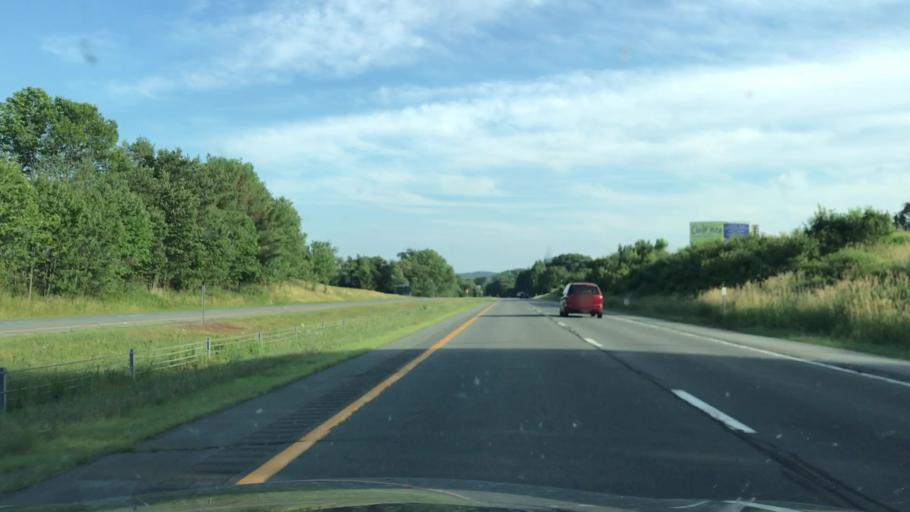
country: US
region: New York
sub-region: Sullivan County
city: Liberty
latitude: 41.7522
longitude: -74.7345
